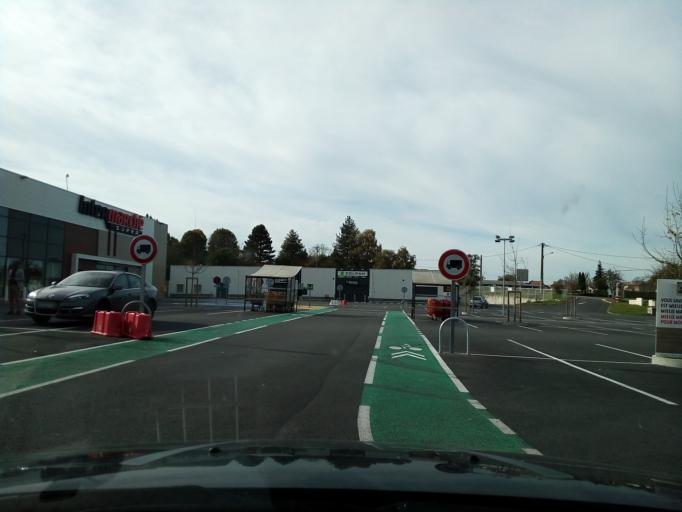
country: FR
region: Limousin
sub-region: Departement de la Creuse
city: Gueret
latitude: 46.1764
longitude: 1.8985
